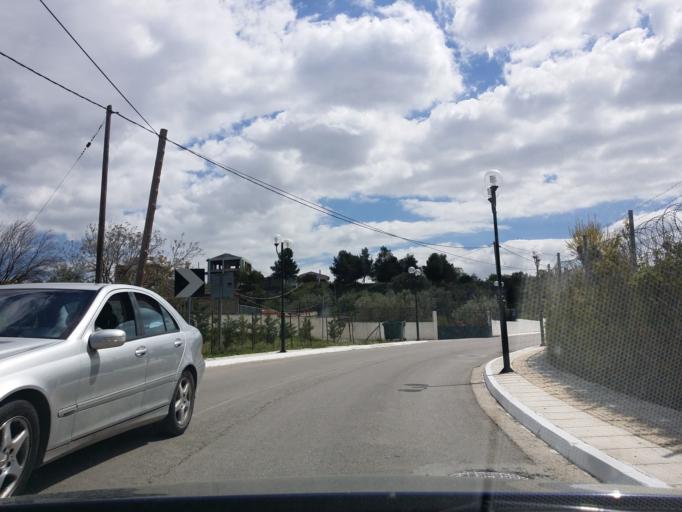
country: GR
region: Attica
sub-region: Nomarchia Dytikis Attikis
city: Fyli
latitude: 38.1085
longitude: 23.6665
